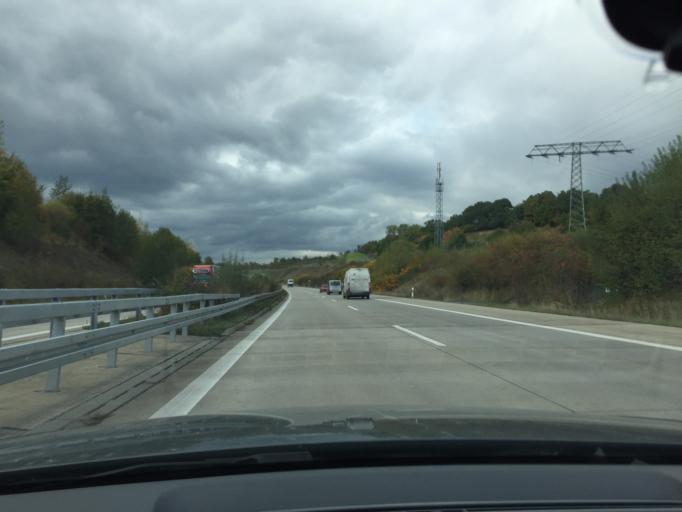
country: DE
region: Saxony
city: Dohna
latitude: 50.9653
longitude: 13.8512
